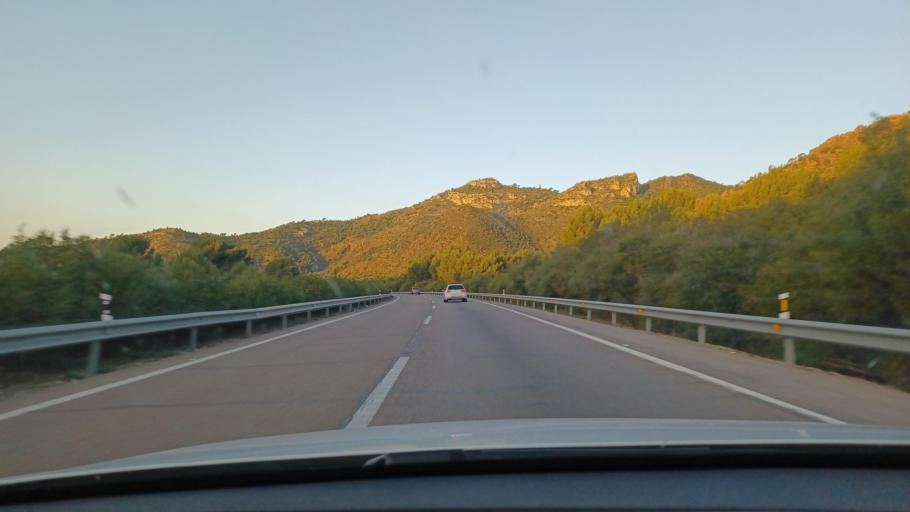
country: ES
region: Valencia
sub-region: Provincia de Castello
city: Benicassim
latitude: 40.0627
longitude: 0.0531
